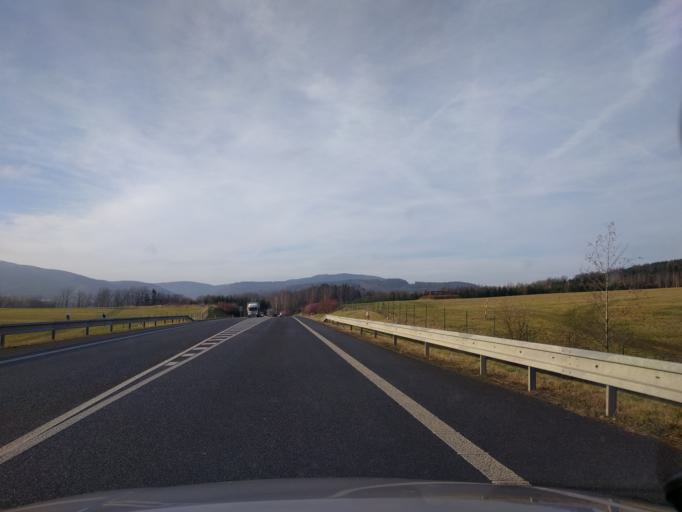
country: CZ
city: Straz nad Nisou
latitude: 50.7961
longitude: 15.0139
